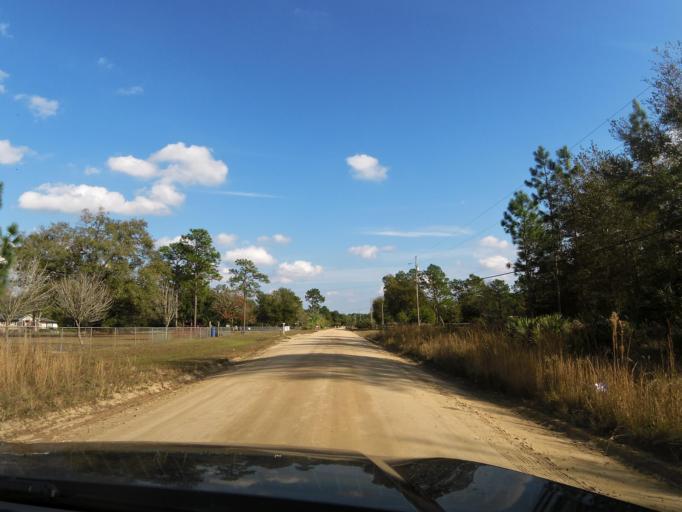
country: US
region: Florida
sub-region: Clay County
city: Middleburg
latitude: 30.1242
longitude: -81.9541
